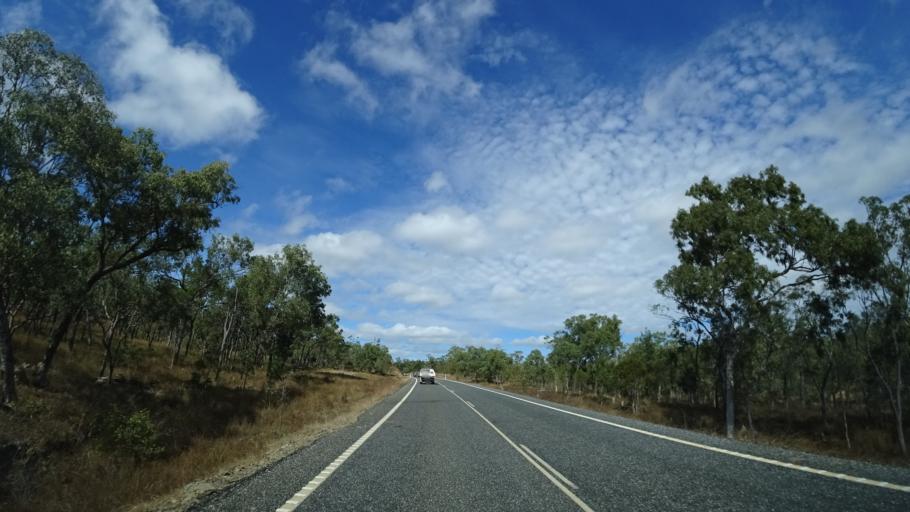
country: AU
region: Queensland
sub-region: Cairns
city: Port Douglas
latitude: -16.2986
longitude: 144.7153
